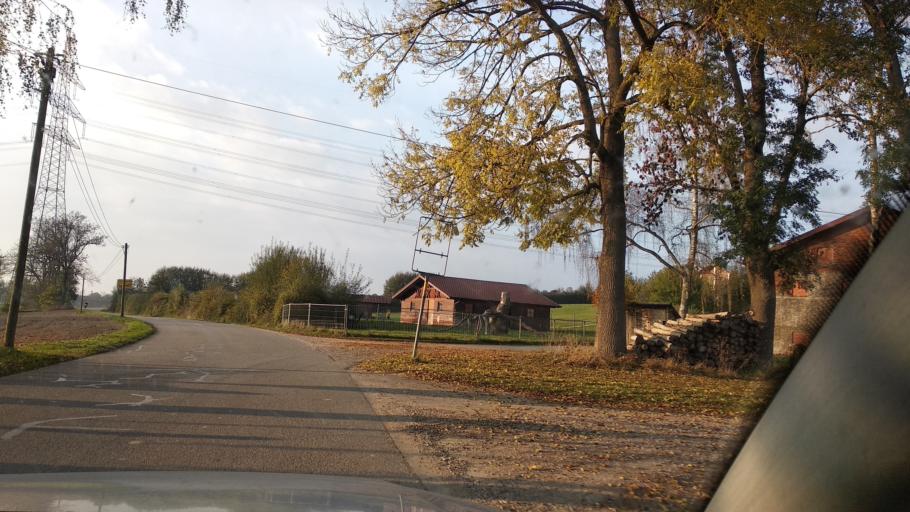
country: DE
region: Bavaria
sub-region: Upper Bavaria
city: Pastetten
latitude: 48.2182
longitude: 11.9220
